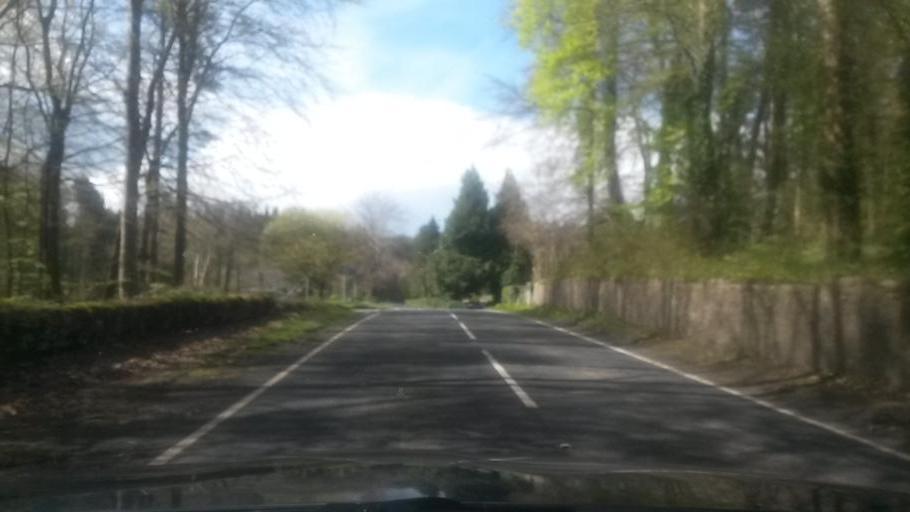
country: GB
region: Northern Ireland
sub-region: Fermanagh District
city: Enniskillen
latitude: 54.3978
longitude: -7.7127
